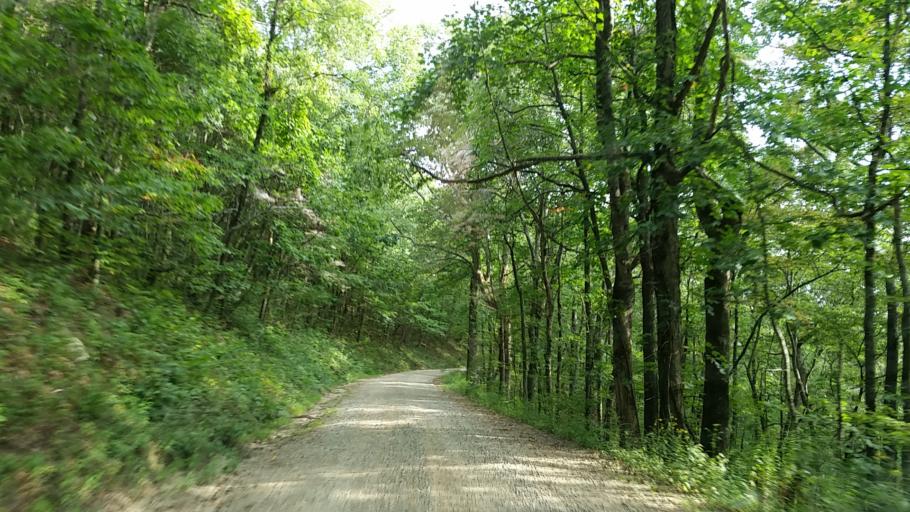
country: US
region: Georgia
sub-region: Lumpkin County
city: Dahlonega
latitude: 34.6518
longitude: -84.0551
